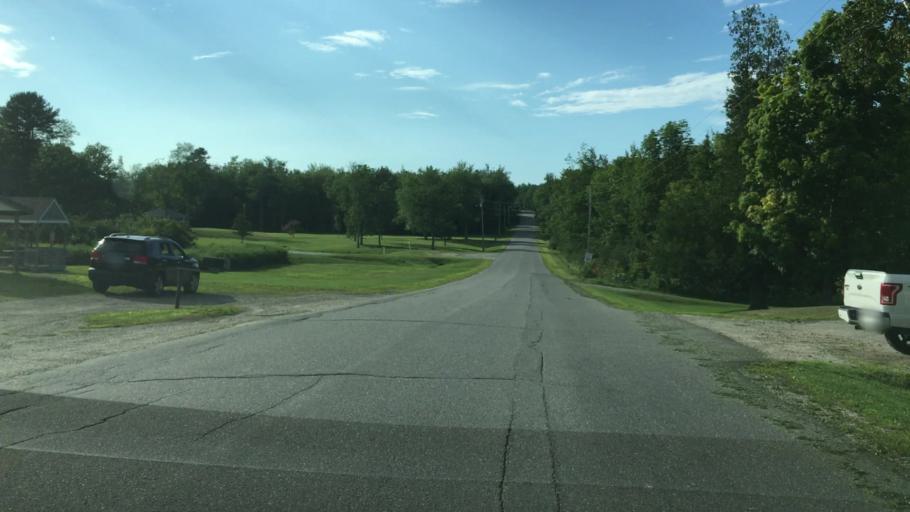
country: US
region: Maine
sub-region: Waldo County
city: Stockton Springs
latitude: 44.4879
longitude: -68.8636
